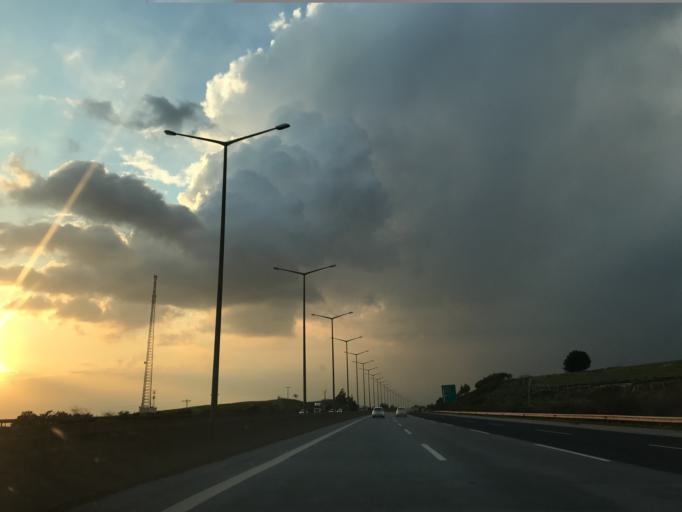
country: TR
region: Adana
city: Seyhan
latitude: 37.0324
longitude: 35.1869
